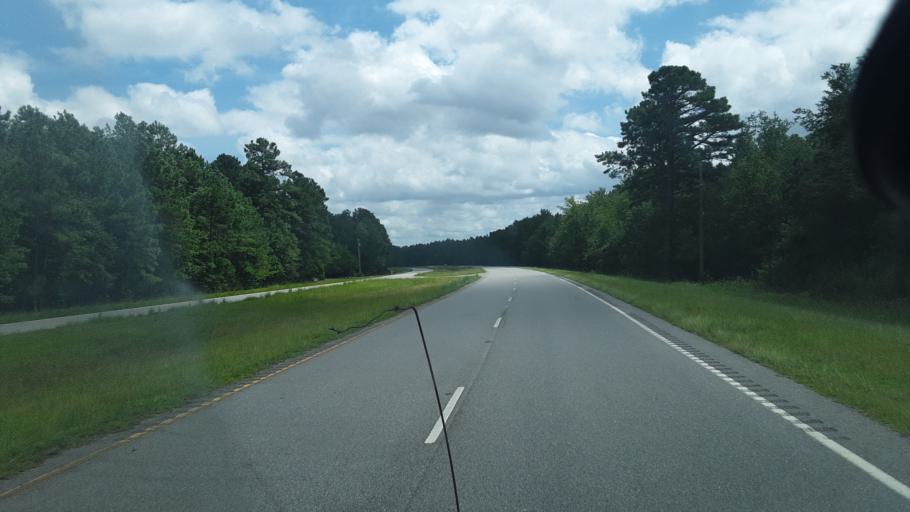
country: US
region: South Carolina
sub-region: Horry County
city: Loris
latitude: 34.0985
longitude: -78.9206
